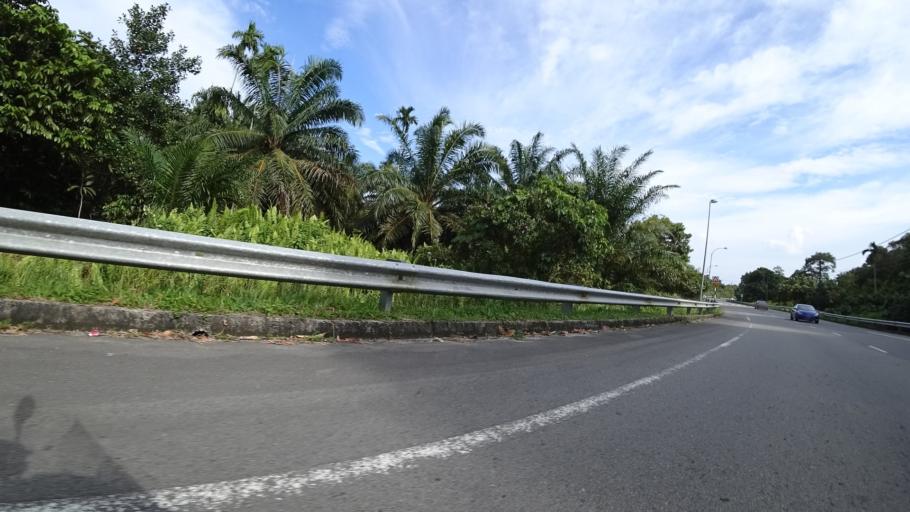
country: BN
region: Brunei and Muara
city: Bandar Seri Begawan
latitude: 4.8816
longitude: 114.8018
